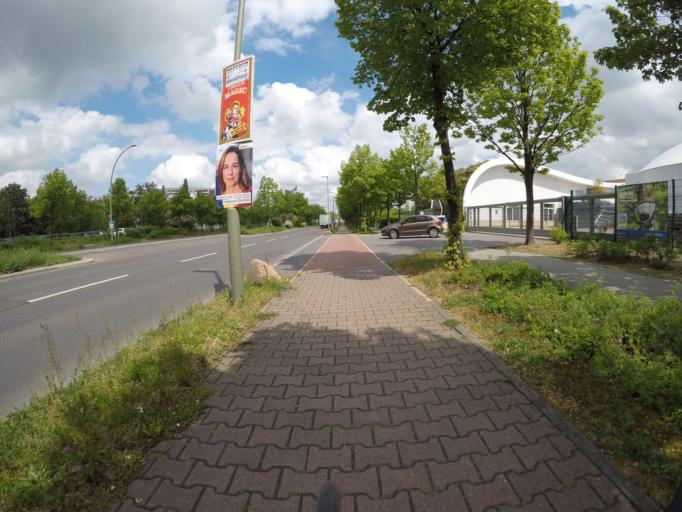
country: DE
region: Berlin
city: Marzahn
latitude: 52.5356
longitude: 13.5672
